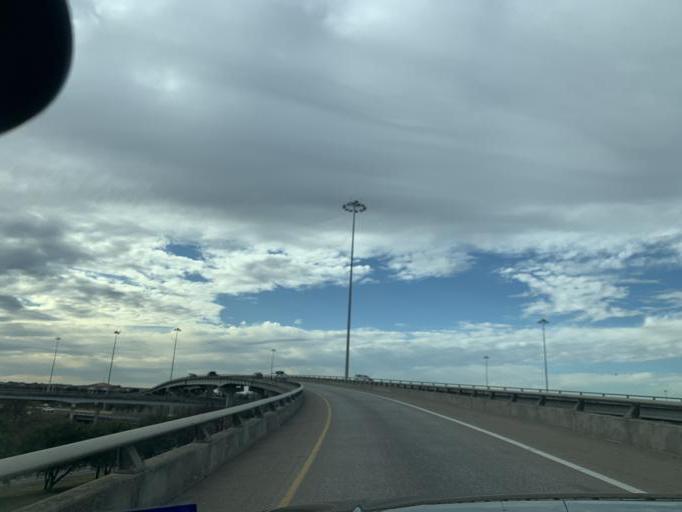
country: US
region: Texas
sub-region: Dallas County
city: Duncanville
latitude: 32.6543
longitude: -96.8756
